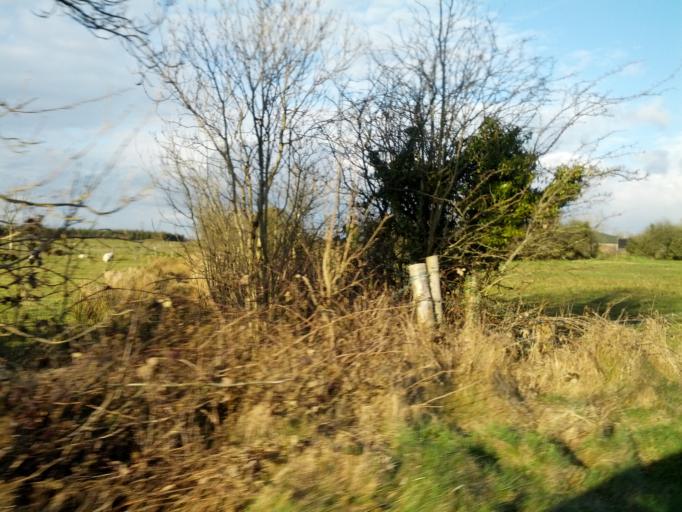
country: IE
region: Connaught
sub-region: County Galway
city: Loughrea
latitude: 53.3805
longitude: -8.5660
